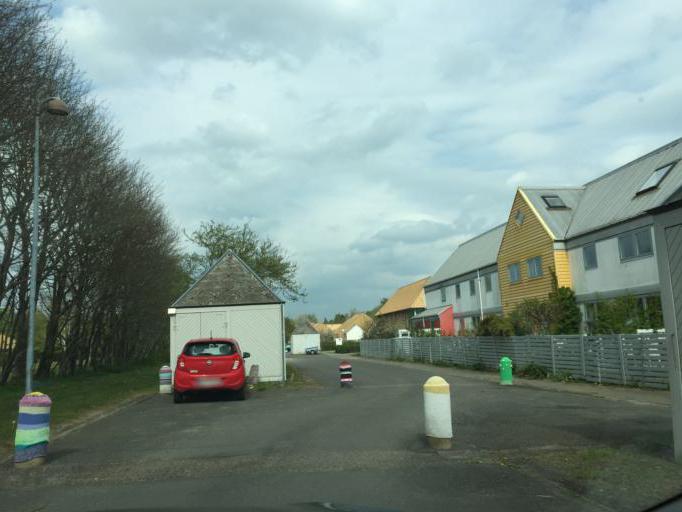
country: DK
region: South Denmark
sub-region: Odense Kommune
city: Neder Holluf
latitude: 55.3815
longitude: 10.4543
